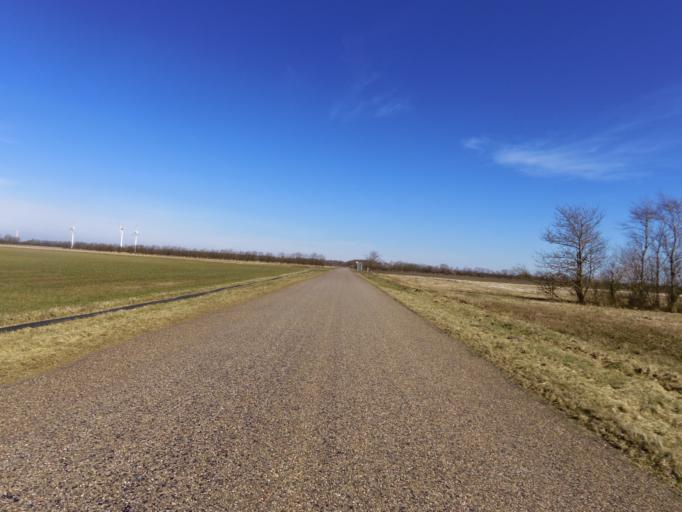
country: DK
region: South Denmark
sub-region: Tonder Kommune
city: Toftlund
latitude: 55.2333
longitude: 9.0667
